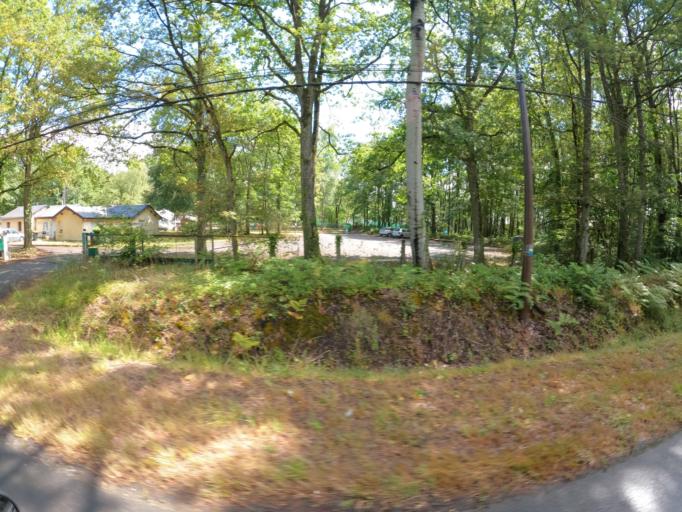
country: FR
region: Pays de la Loire
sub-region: Departement de Maine-et-Loire
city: Feneu
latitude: 47.5812
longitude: -0.5917
